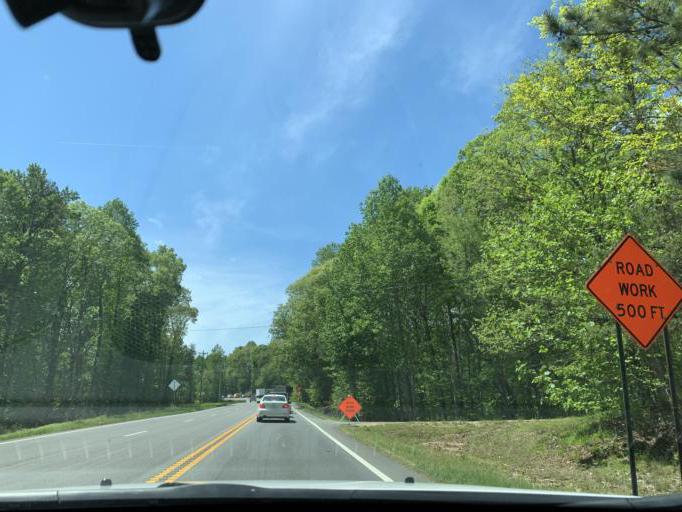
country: US
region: Georgia
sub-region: Forsyth County
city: Cumming
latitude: 34.2472
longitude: -84.0282
